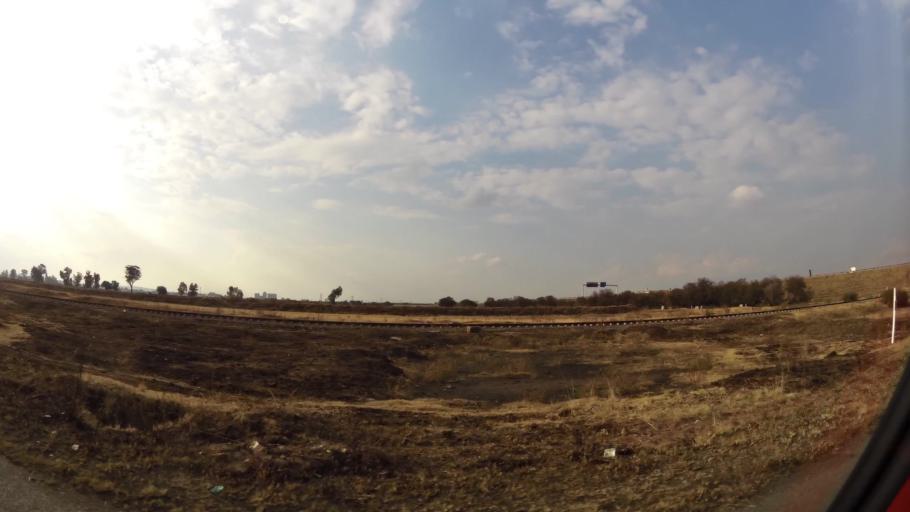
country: ZA
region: Gauteng
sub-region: Sedibeng District Municipality
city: Vereeniging
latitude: -26.6777
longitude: 27.9018
